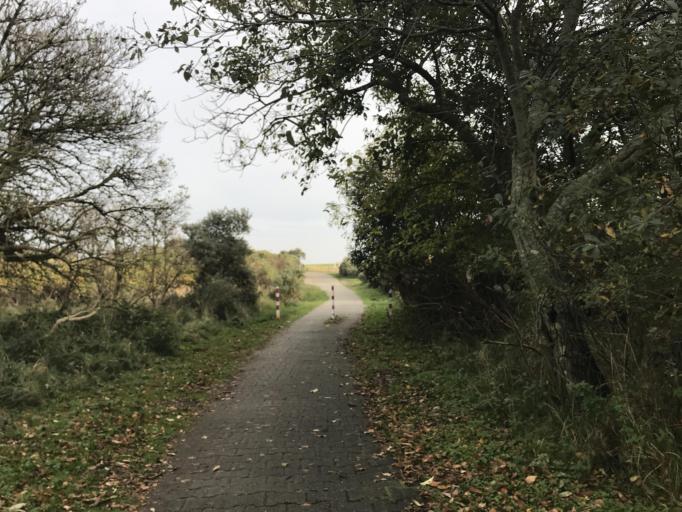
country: DE
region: Lower Saxony
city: Borkum
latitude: 53.6032
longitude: 6.7630
